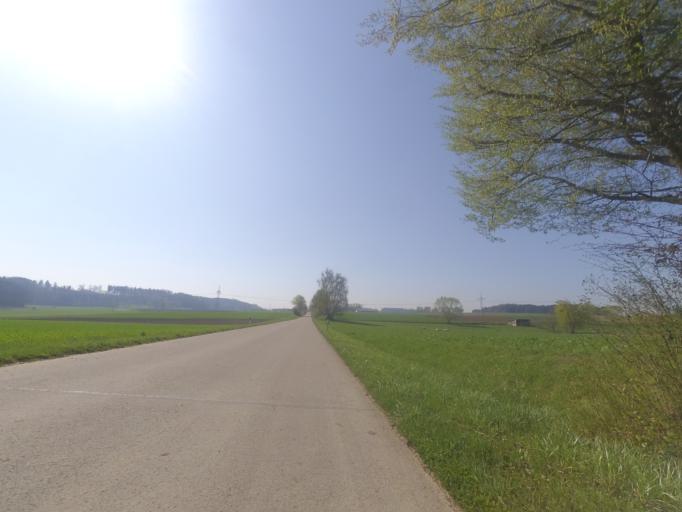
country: DE
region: Bavaria
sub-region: Swabia
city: Pfaffenhofen an der Roth
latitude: 48.3925
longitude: 10.1741
